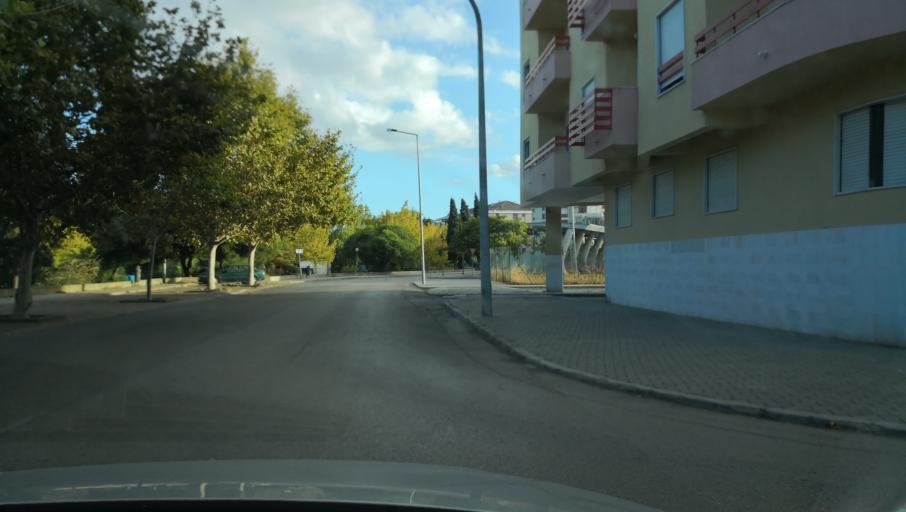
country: PT
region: Setubal
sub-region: Moita
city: Alhos Vedros
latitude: 38.6657
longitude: -9.0448
